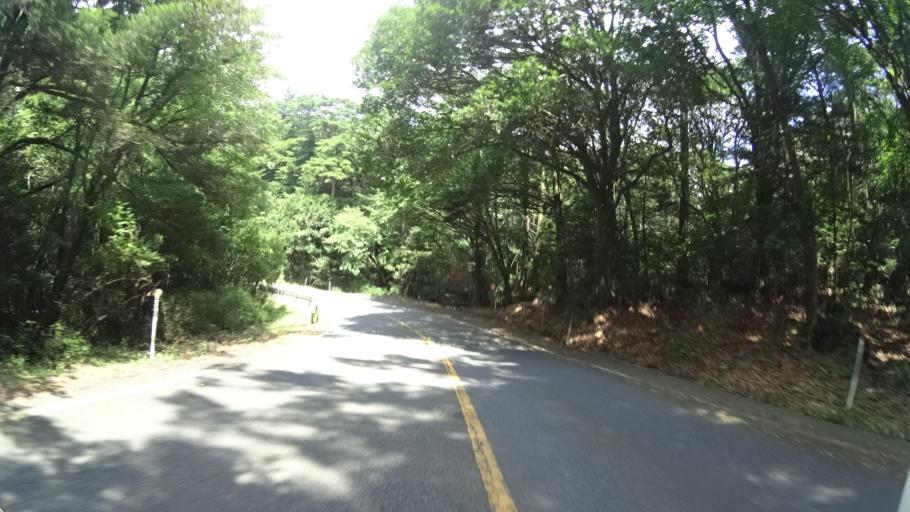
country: JP
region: Miyazaki
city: Kobayashi
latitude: 31.9005
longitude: 130.8492
